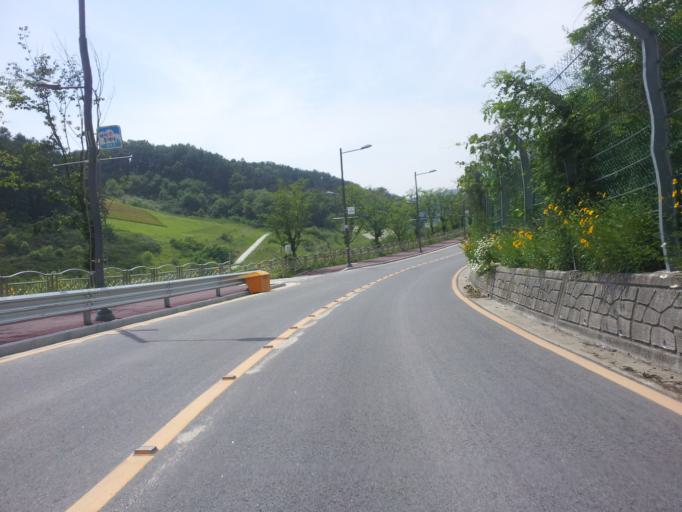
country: KR
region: Daejeon
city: Sintansin
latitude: 36.4561
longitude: 127.4723
